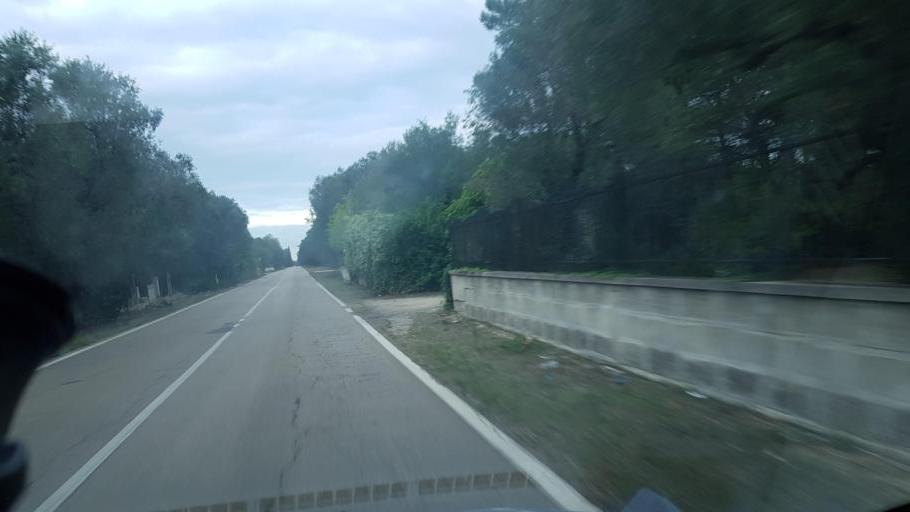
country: IT
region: Apulia
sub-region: Provincia di Brindisi
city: Latiano
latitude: 40.5276
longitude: 17.6847
